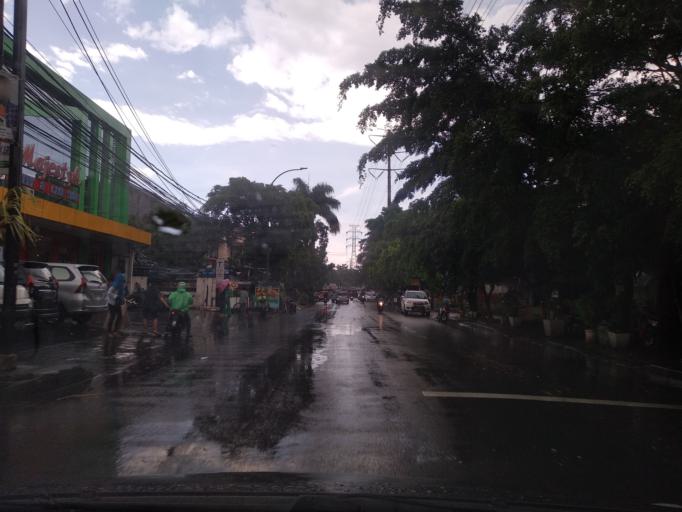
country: ID
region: Jakarta Raya
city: Jakarta
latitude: -6.2198
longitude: 106.8867
